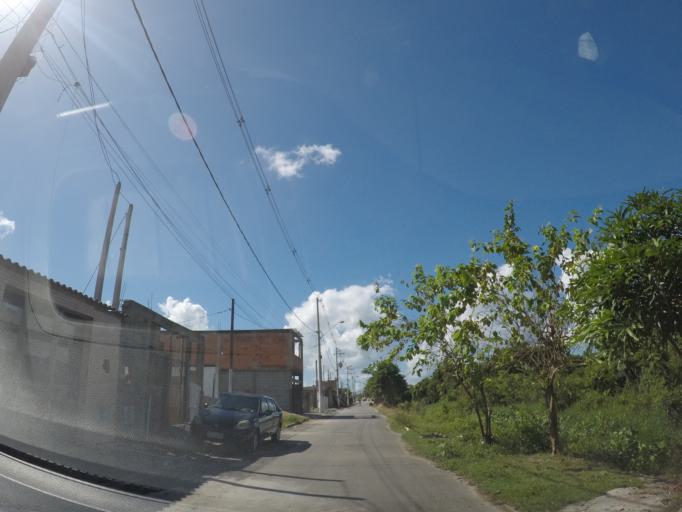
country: BR
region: Sao Paulo
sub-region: Praia Grande
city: Praia Grande
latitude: -24.0187
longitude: -46.5142
